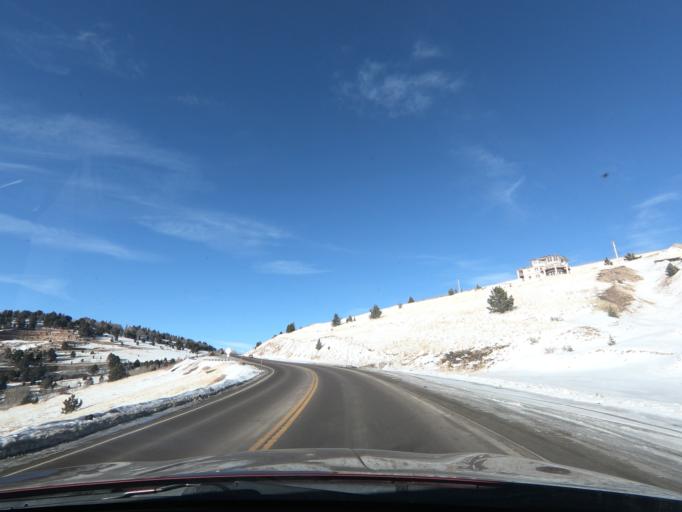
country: US
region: Colorado
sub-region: Teller County
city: Cripple Creek
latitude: 38.7579
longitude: -105.1620
